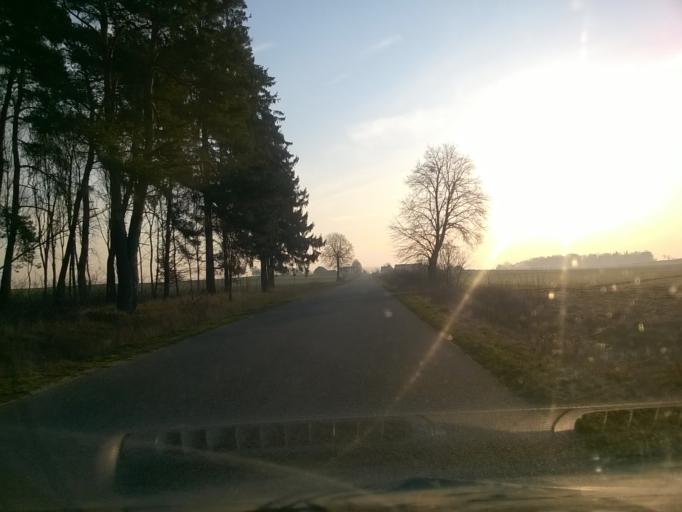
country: PL
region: Kujawsko-Pomorskie
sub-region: Powiat tucholski
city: Gostycyn
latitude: 53.4798
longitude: 17.7310
